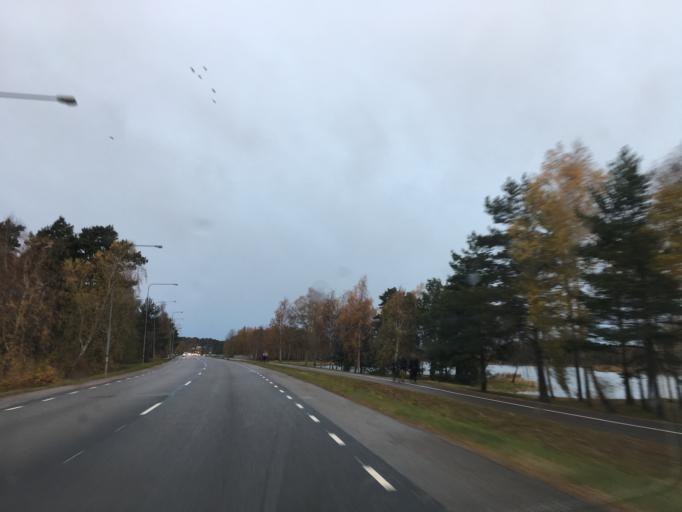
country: SE
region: Kalmar
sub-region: Kalmar Kommun
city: Kalmar
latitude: 56.6750
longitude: 16.3650
